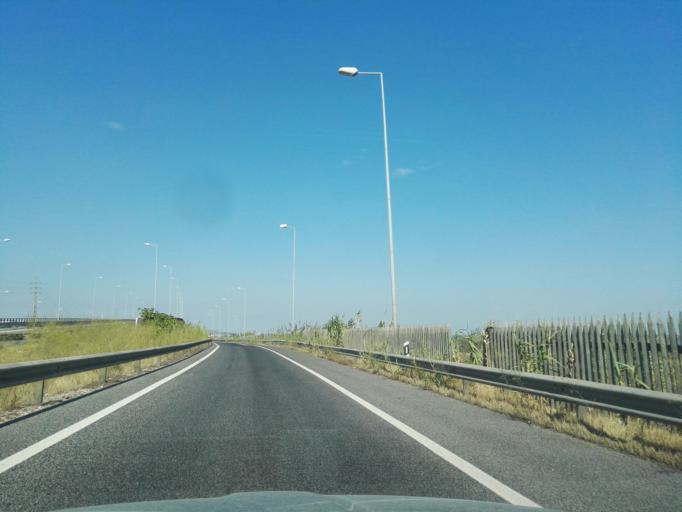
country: PT
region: Lisbon
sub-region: Loures
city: Santa Iria da Azoia
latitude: 38.8326
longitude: -9.0776
